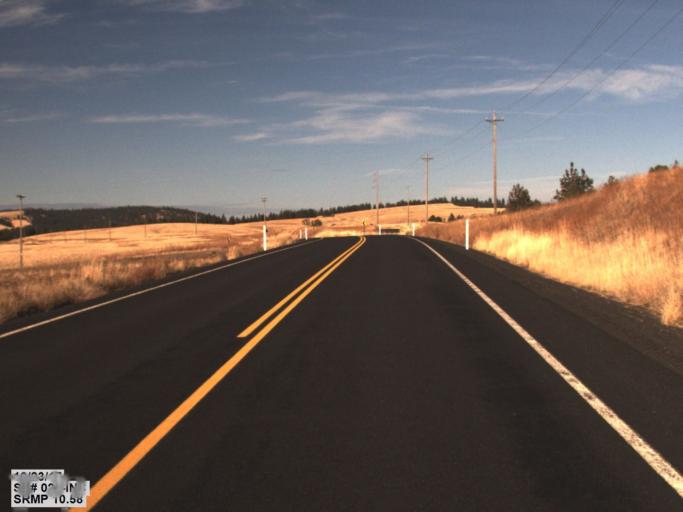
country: US
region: Washington
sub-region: Lincoln County
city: Davenport
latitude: 47.8016
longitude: -118.1737
